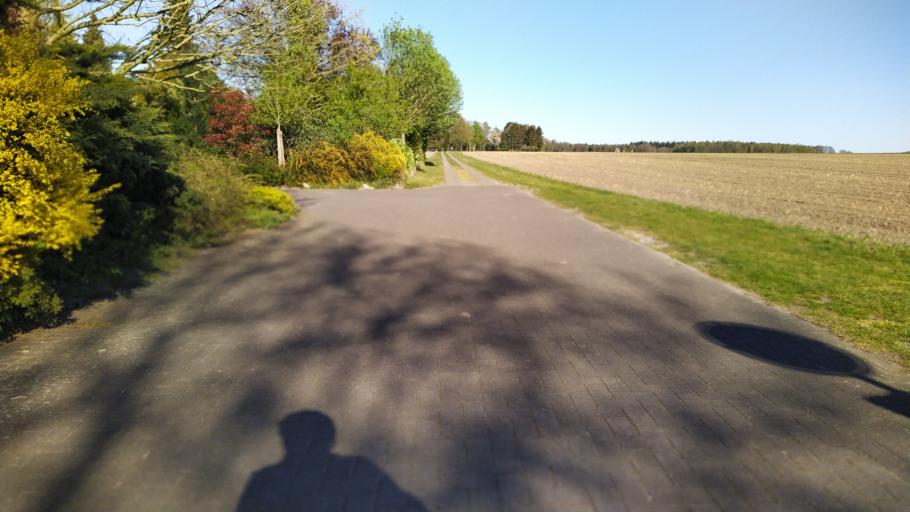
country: DE
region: Lower Saxony
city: Klein Meckelsen
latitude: 53.2937
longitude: 9.4487
